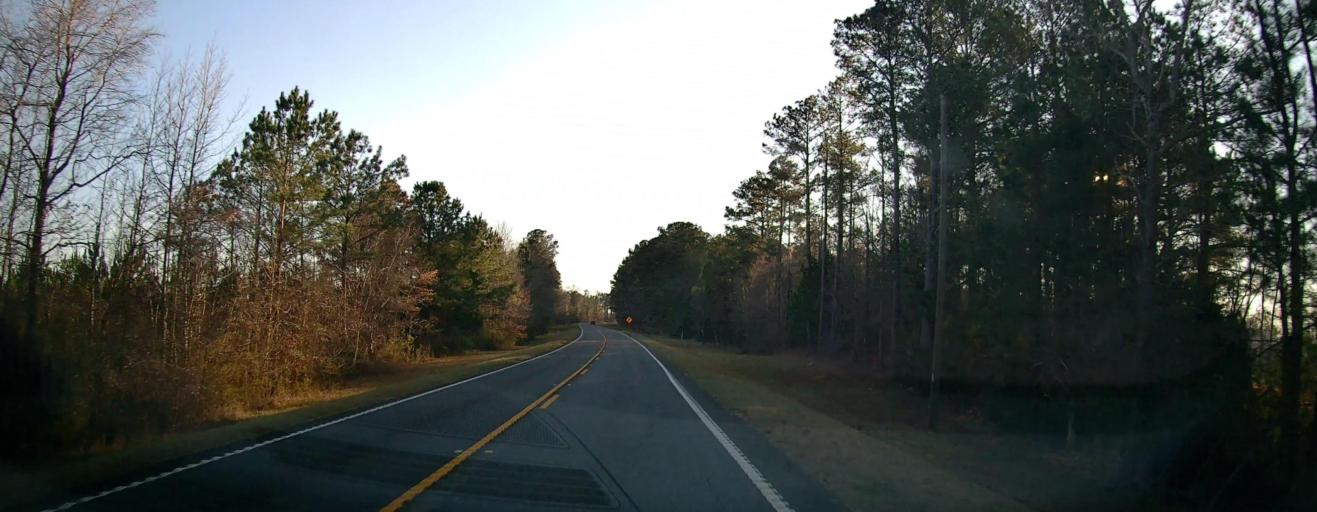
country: US
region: Georgia
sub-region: Talbot County
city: Talbotton
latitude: 32.6687
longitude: -84.6156
